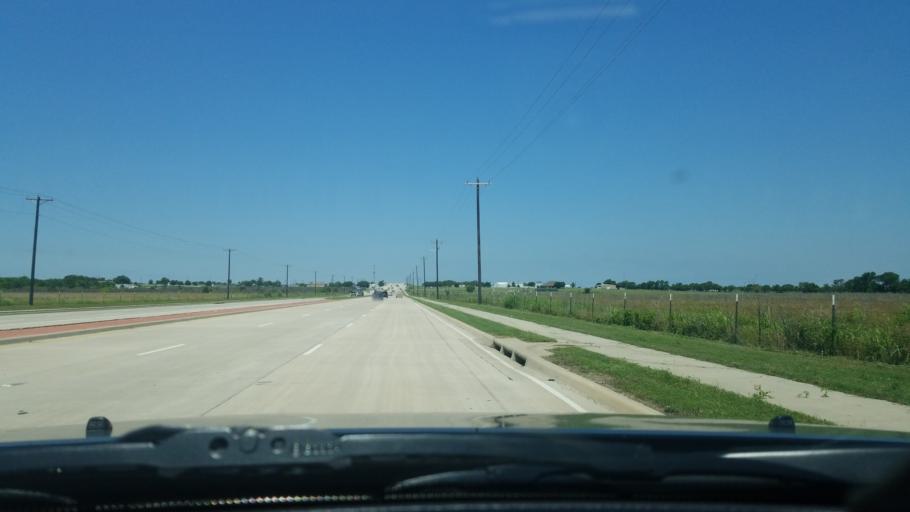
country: US
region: Texas
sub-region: Denton County
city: Krum
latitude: 33.2336
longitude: -97.2346
